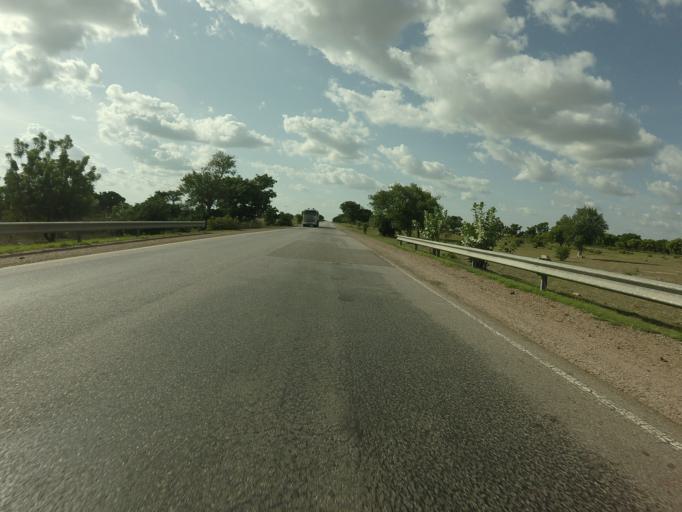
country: GH
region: Upper East
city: Bolgatanga
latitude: 10.6586
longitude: -0.8590
